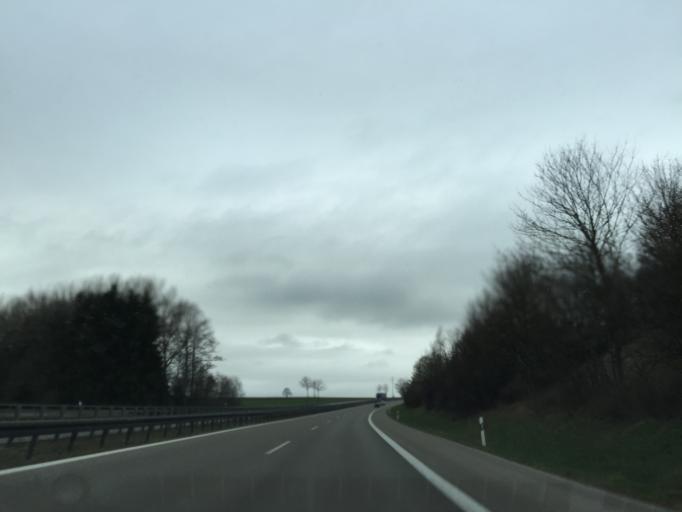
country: DE
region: Baden-Wuerttemberg
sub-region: Freiburg Region
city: Bad Durrheim
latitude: 48.0156
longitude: 8.5250
